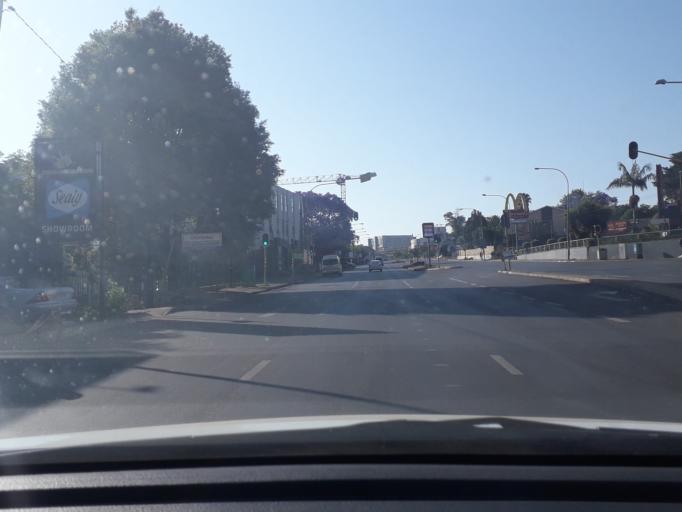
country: ZA
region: Gauteng
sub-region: City of Johannesburg Metropolitan Municipality
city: Johannesburg
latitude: -26.1163
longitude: 28.0238
